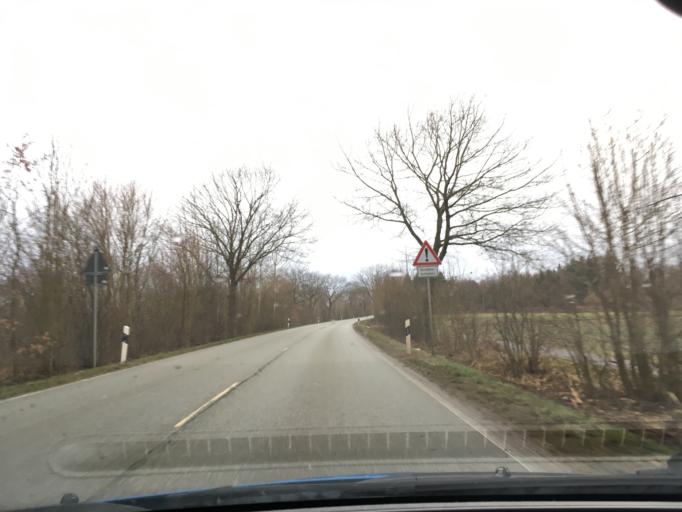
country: DE
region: Schleswig-Holstein
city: Siebeneichen
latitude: 53.4978
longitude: 10.6127
